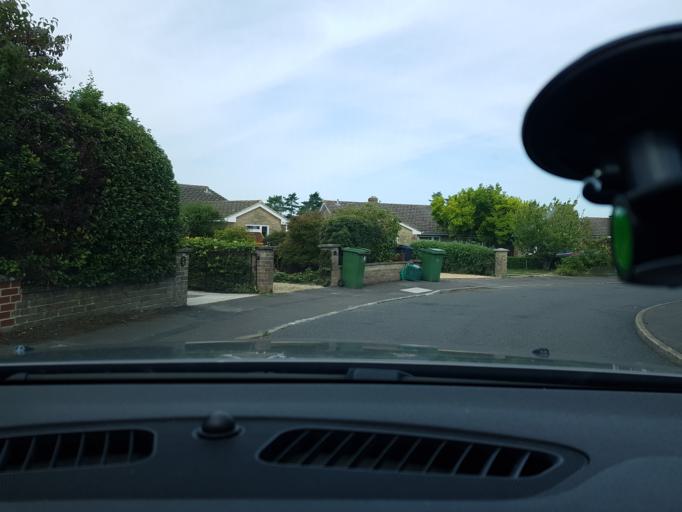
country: GB
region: England
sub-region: West Berkshire
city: Hungerford
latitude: 51.4102
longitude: -1.5222
